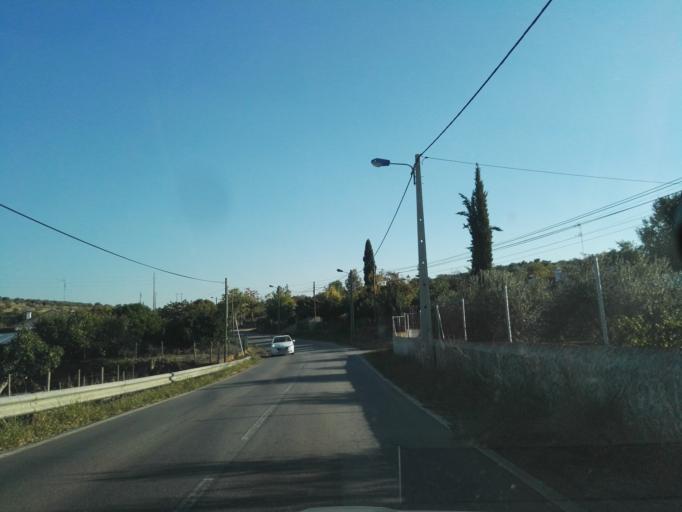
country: PT
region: Portalegre
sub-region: Elvas
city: Elvas
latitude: 38.8950
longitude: -7.1729
